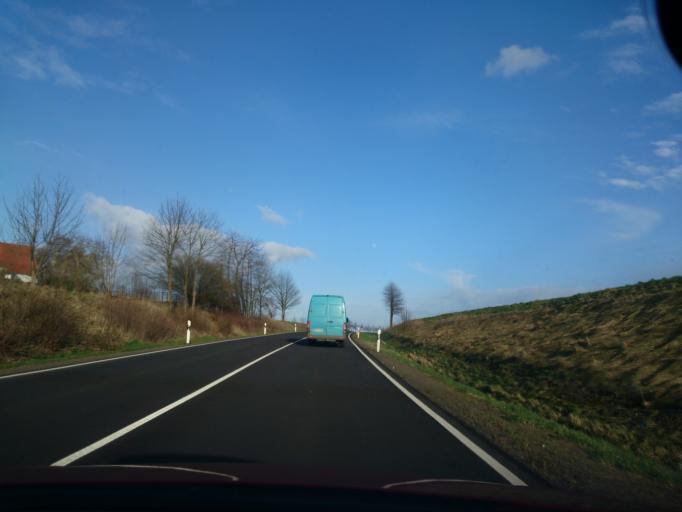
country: DE
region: Mecklenburg-Vorpommern
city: Brandshagen
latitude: 54.2359
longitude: 13.1823
